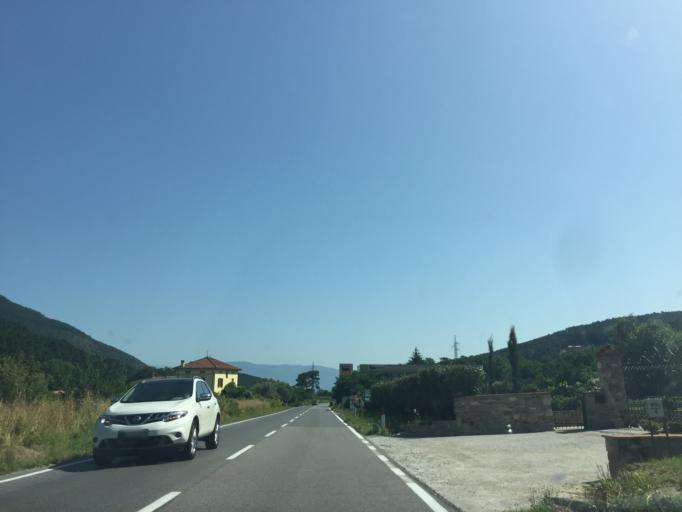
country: IT
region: Tuscany
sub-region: Province of Pisa
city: Asciano
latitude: 43.7818
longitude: 10.4639
